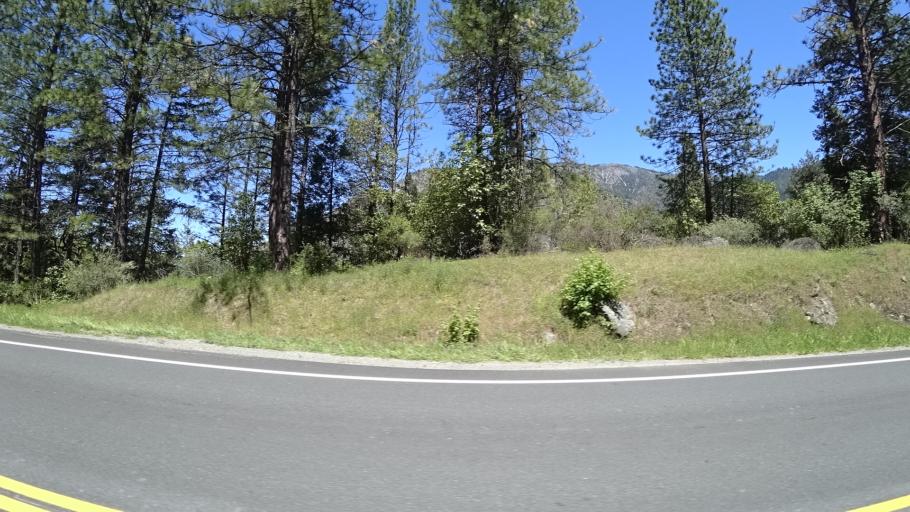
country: US
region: California
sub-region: Humboldt County
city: Willow Creek
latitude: 40.8072
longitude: -123.4721
